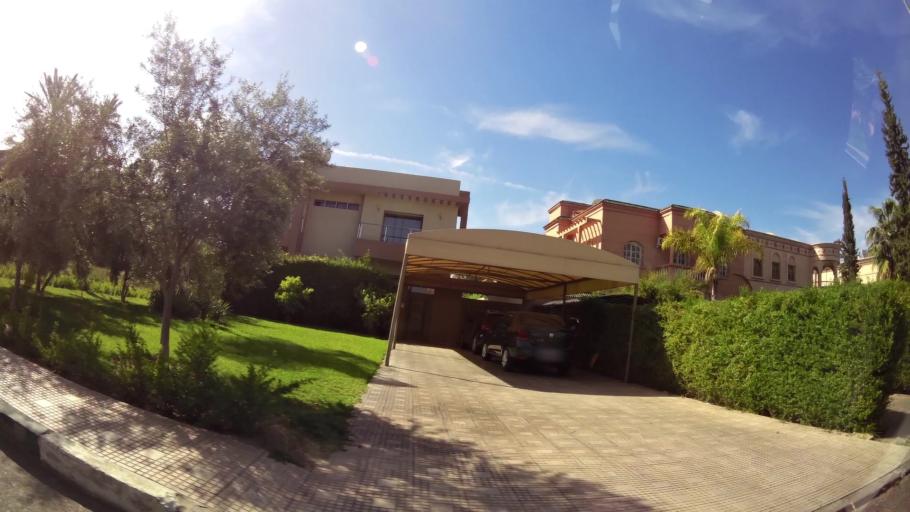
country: MA
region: Marrakech-Tensift-Al Haouz
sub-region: Marrakech
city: Marrakesh
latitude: 31.6513
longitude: -8.0513
